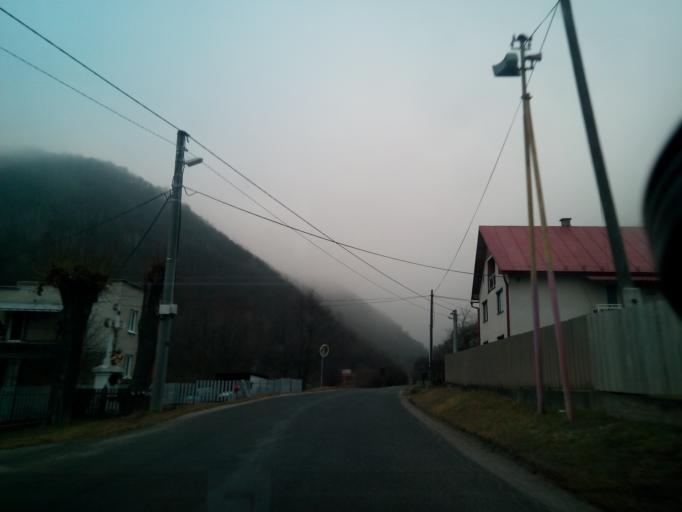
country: SK
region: Kosicky
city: Krompachy
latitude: 48.9391
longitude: 20.9427
